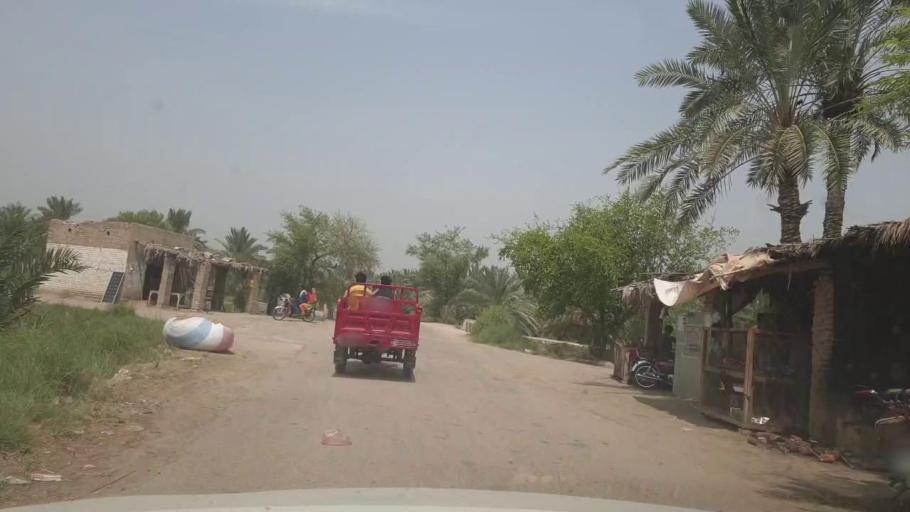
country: PK
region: Sindh
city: Kot Diji
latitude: 27.3629
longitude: 68.6965
